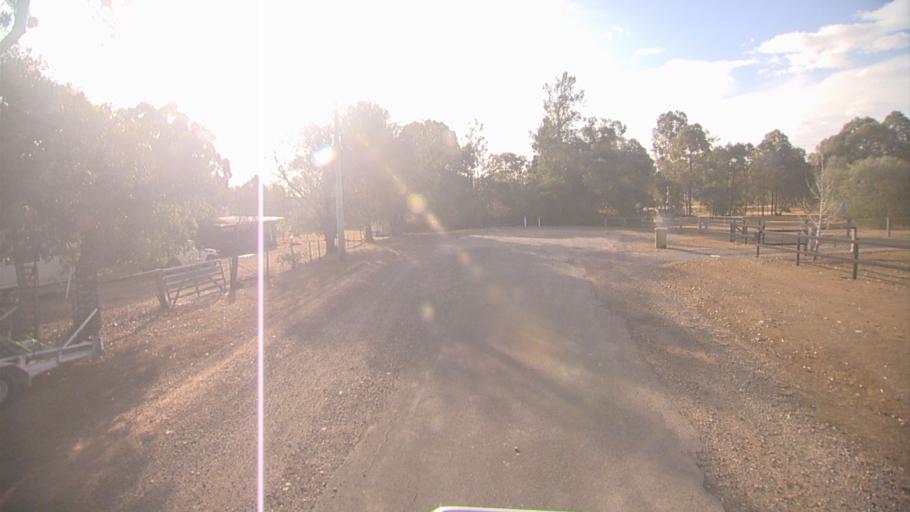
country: AU
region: Queensland
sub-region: Logan
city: Cedar Vale
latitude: -27.8778
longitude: 153.0207
